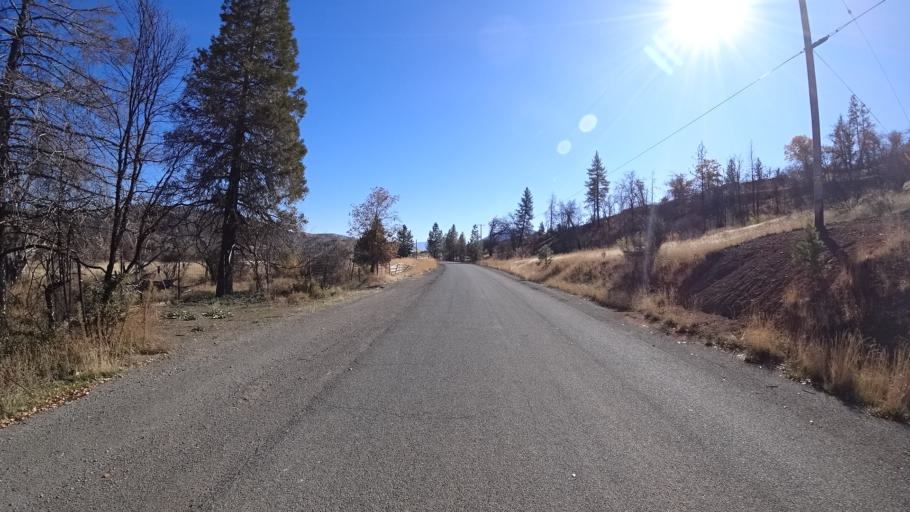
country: US
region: California
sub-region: Siskiyou County
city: Yreka
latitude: 41.9311
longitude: -122.5877
